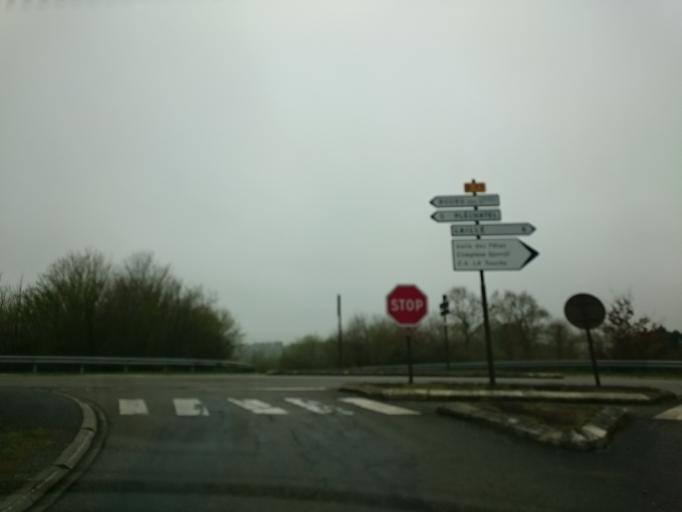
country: FR
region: Brittany
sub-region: Departement d'Ille-et-Vilaine
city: Bourg-des-Comptes
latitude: 47.9324
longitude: -1.7319
